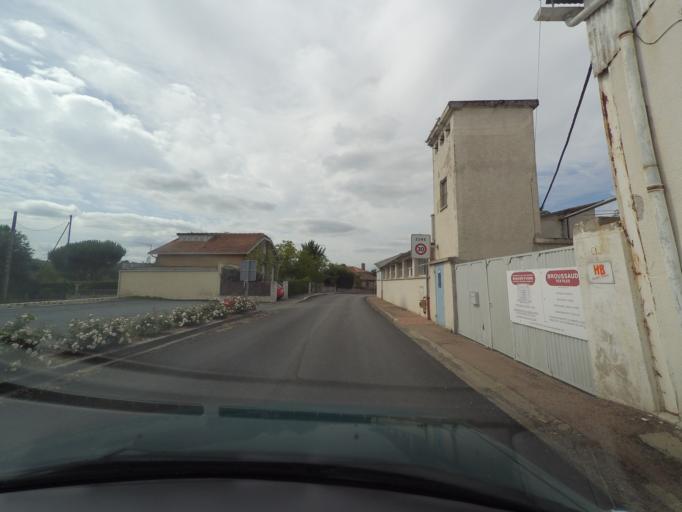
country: FR
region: Limousin
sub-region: Departement de la Haute-Vienne
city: Bussiere-Galant
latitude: 45.6775
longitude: 1.0745
